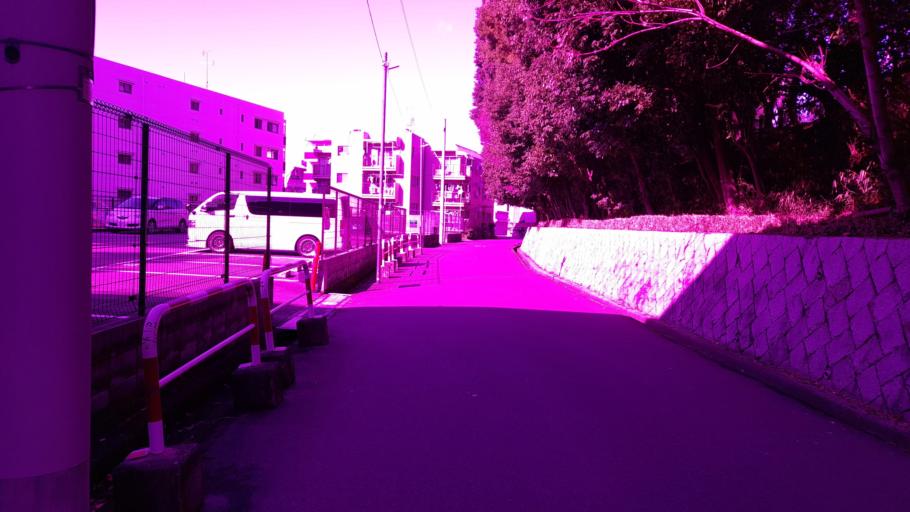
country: JP
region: Osaka
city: Toyonaka
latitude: 34.7604
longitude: 135.4494
